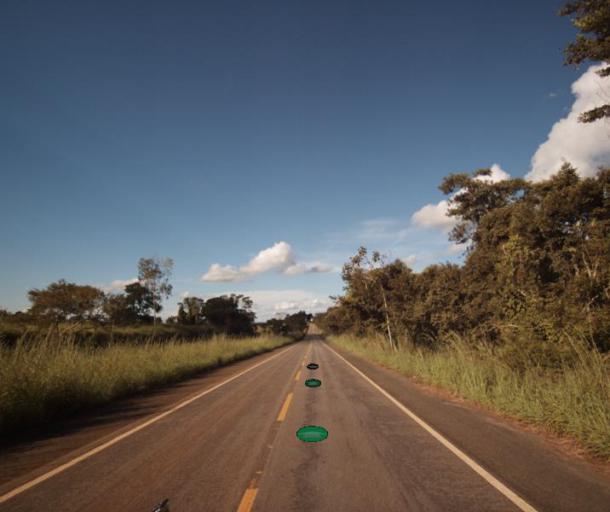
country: BR
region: Goias
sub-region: Itaberai
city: Itaberai
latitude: -15.9797
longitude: -49.6860
